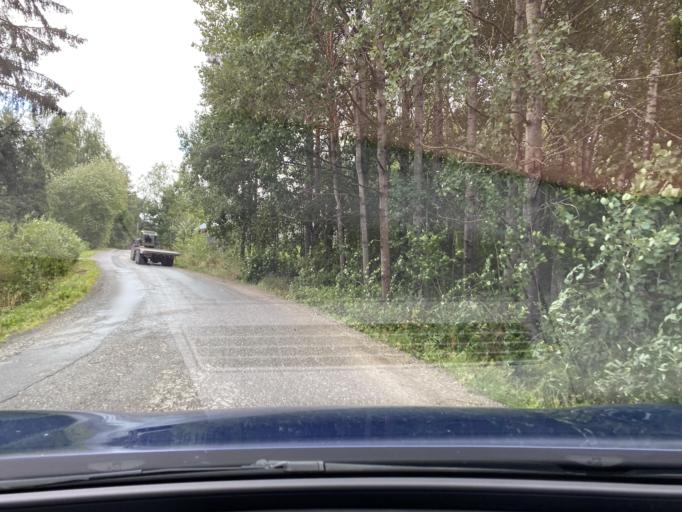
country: FI
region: Pirkanmaa
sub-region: Lounais-Pirkanmaa
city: Punkalaidun
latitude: 61.1686
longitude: 23.1781
